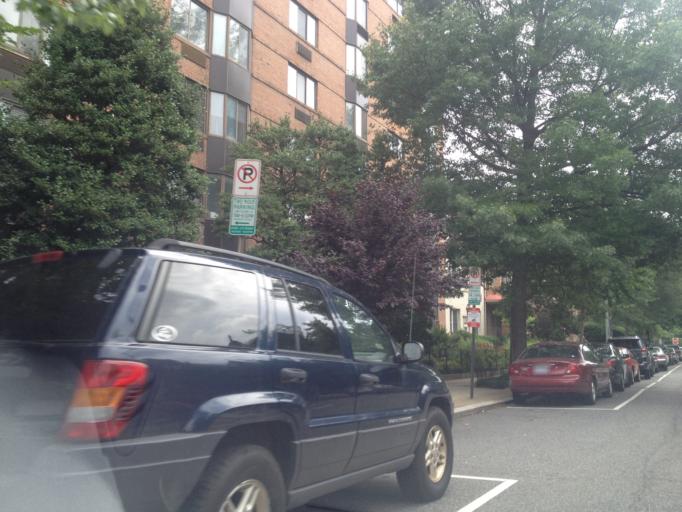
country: US
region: Washington, D.C.
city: Washington, D.C.
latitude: 38.9156
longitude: -77.0431
